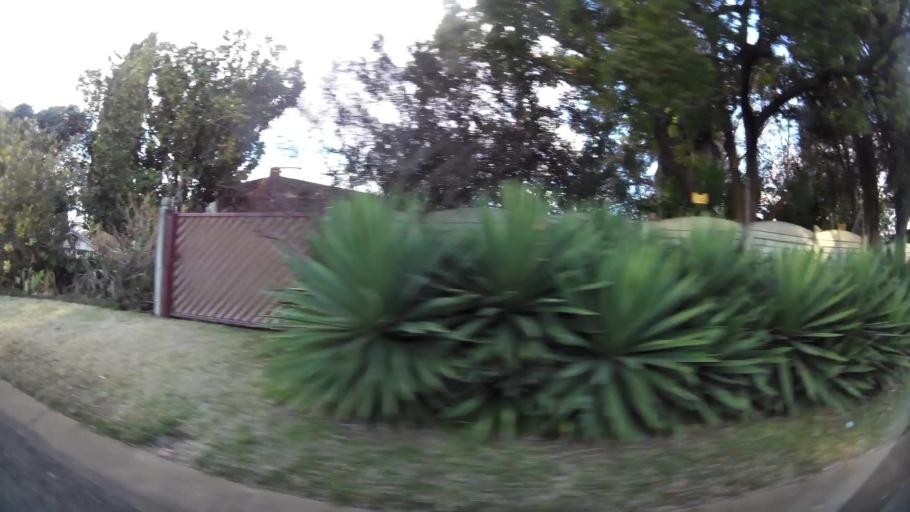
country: ZA
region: North-West
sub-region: Dr Kenneth Kaunda District Municipality
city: Potchefstroom
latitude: -26.7204
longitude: 27.0834
